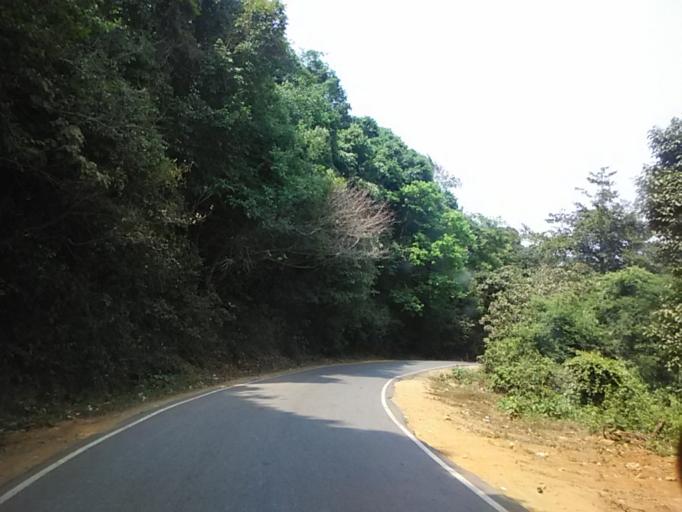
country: IN
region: Karnataka
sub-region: Kodagu
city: Virarajendrapet
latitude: 12.1414
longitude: 75.7945
